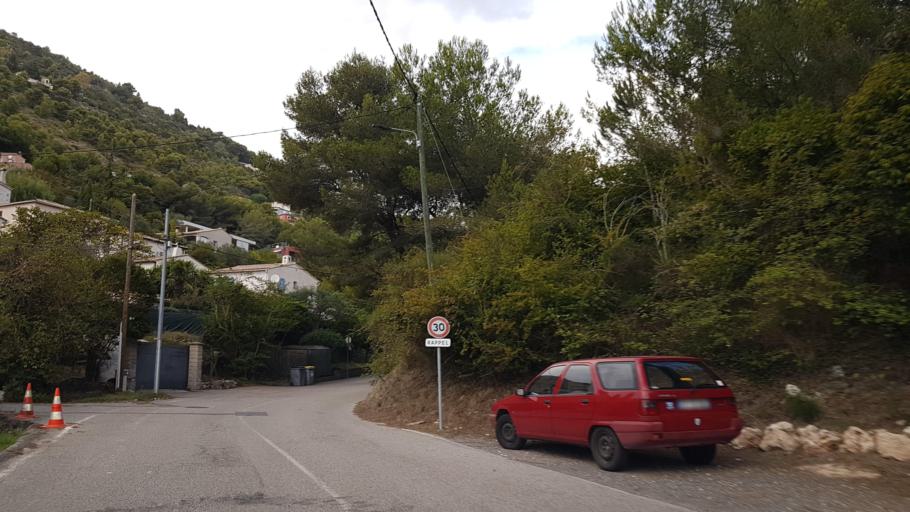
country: FR
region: Provence-Alpes-Cote d'Azur
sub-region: Departement des Alpes-Maritimes
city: La Turbie
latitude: 43.7359
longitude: 7.3940
